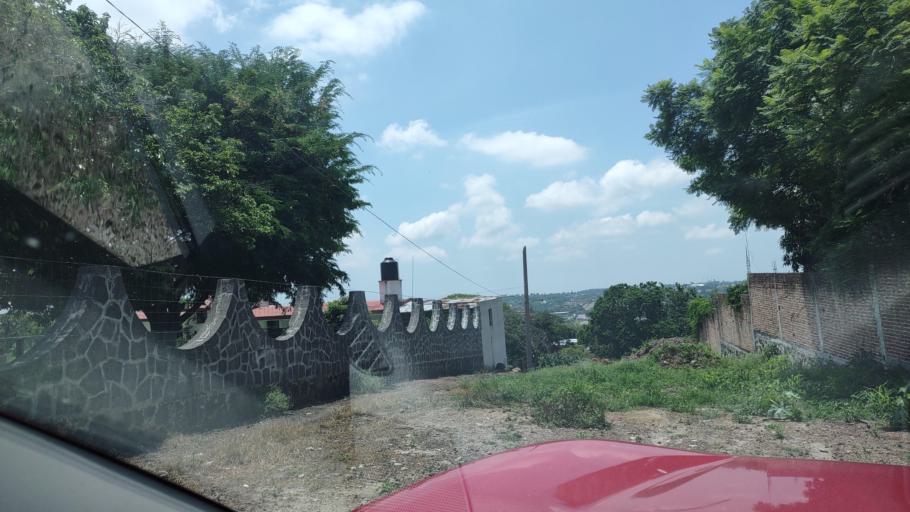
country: MX
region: Veracruz
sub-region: Emiliano Zapata
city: Dos Rios
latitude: 19.4890
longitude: -96.8141
